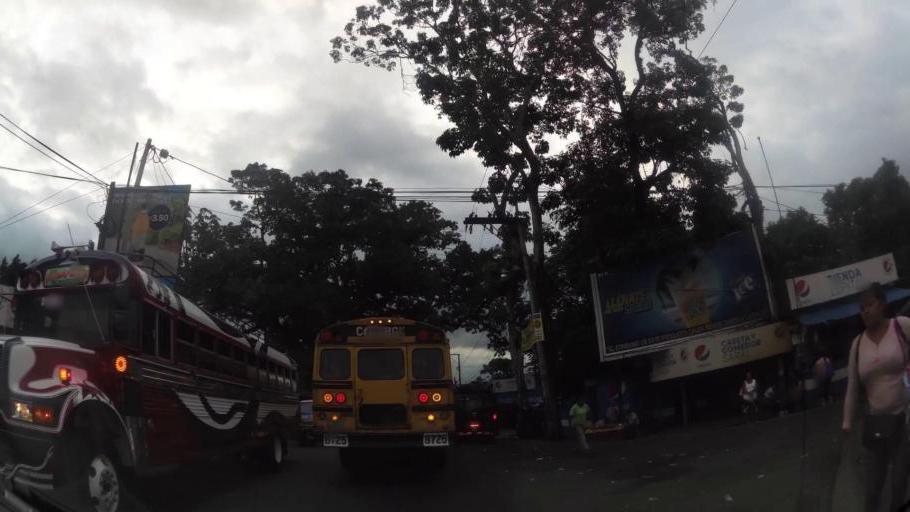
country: GT
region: Suchitepeque
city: Patulul
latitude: 14.3652
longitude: -91.0994
